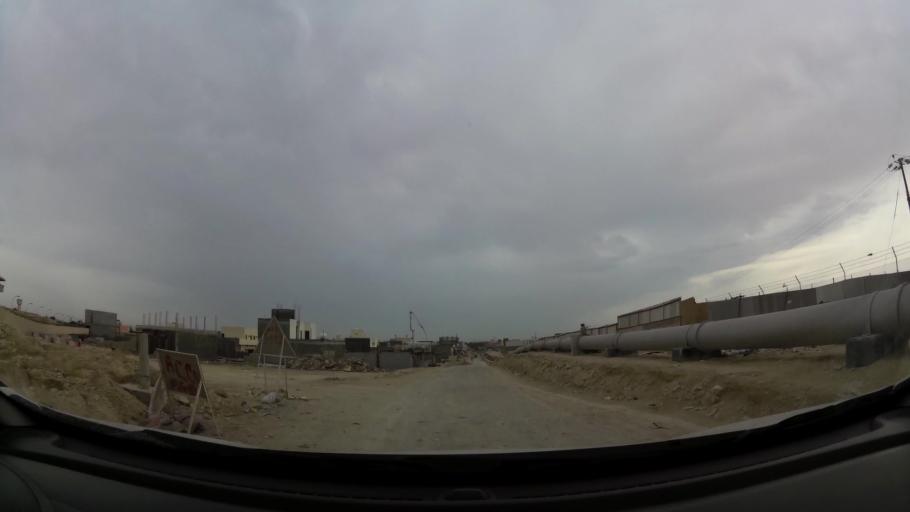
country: BH
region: Central Governorate
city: Madinat Hamad
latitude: 26.1438
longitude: 50.4811
